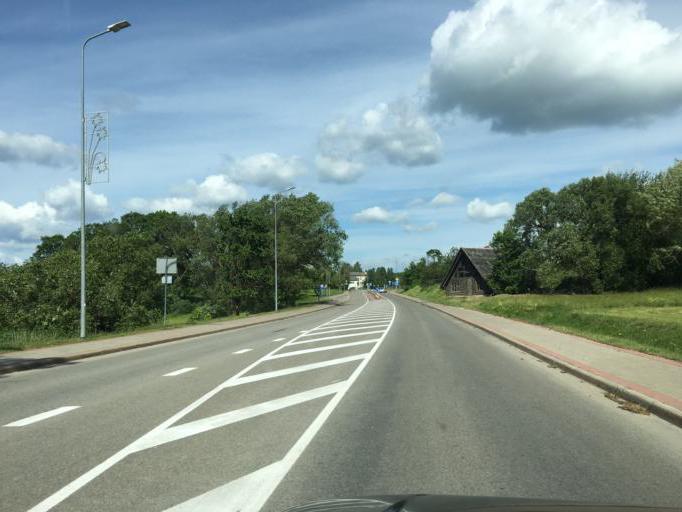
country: LV
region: Balvu Rajons
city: Balvi
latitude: 57.1377
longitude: 27.2558
